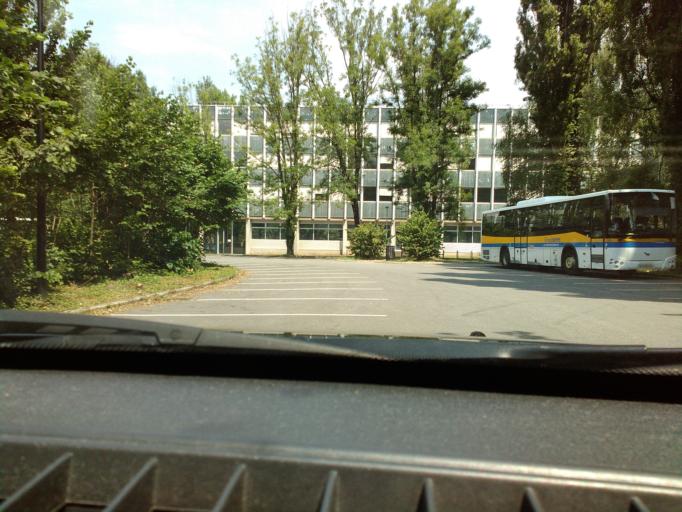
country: FR
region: Rhone-Alpes
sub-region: Departement de l'Isere
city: Corenc
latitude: 45.1954
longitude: 5.7686
